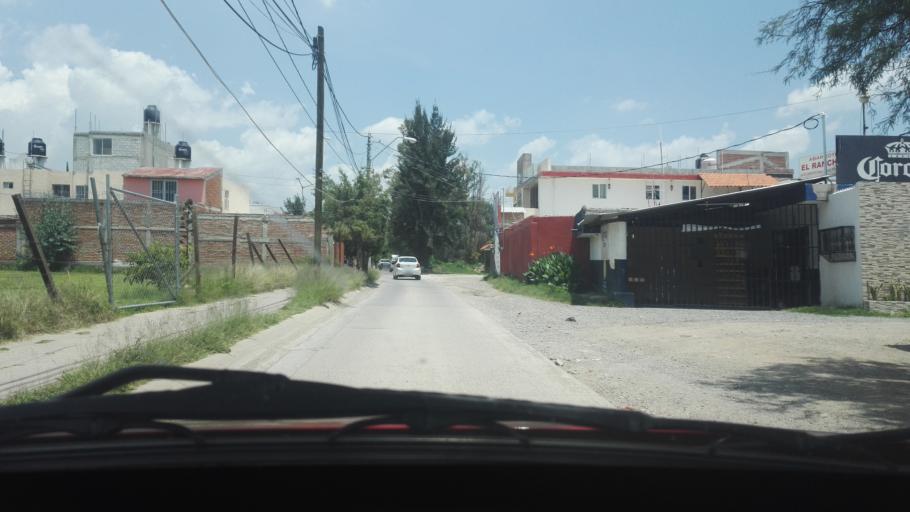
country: MX
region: Guanajuato
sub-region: Leon
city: Fraccionamiento Paraiso Real
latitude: 21.0698
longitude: -101.6061
